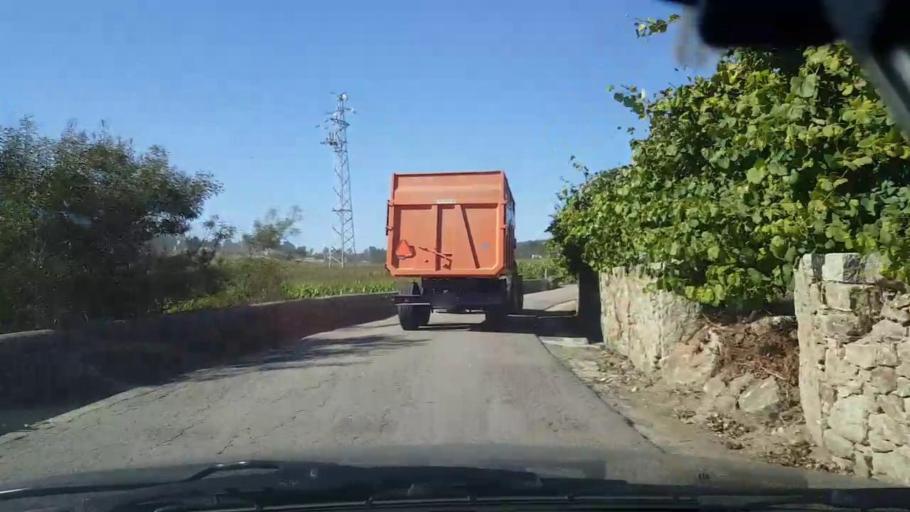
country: PT
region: Braga
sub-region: Vila Nova de Famalicao
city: Ribeirao
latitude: 41.3595
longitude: -8.6432
